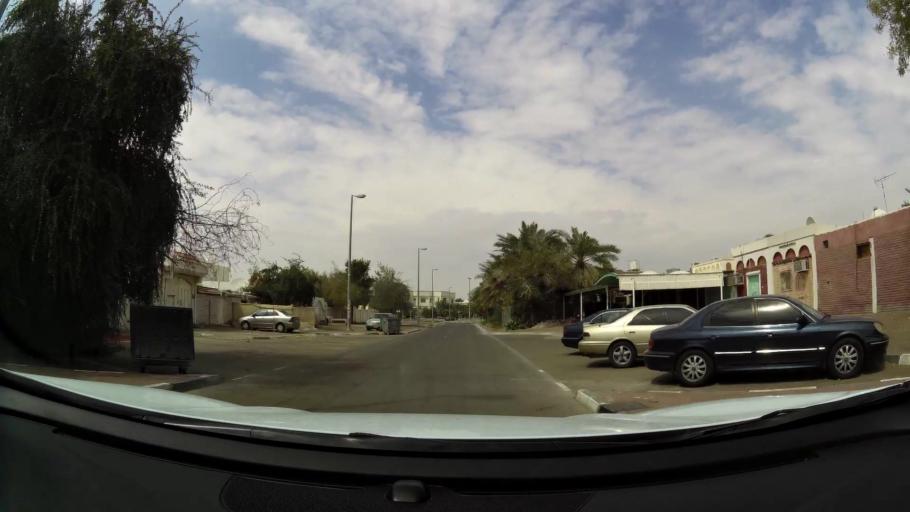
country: AE
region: Abu Dhabi
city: Al Ain
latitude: 24.1985
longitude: 55.7893
